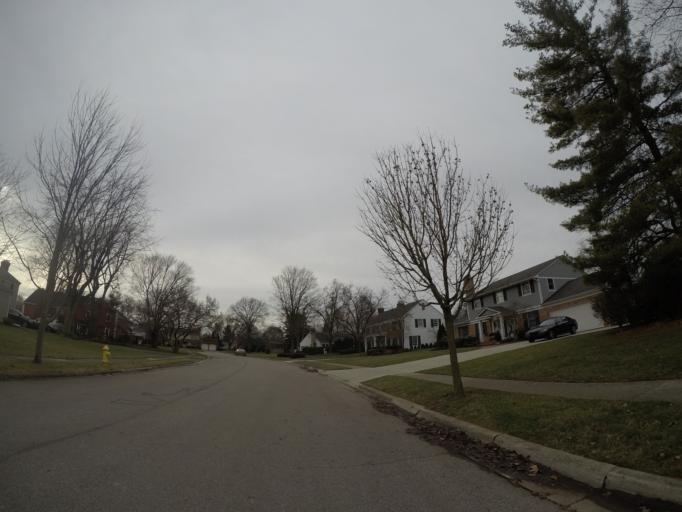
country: US
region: Ohio
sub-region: Franklin County
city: Upper Arlington
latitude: 40.0311
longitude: -83.0694
